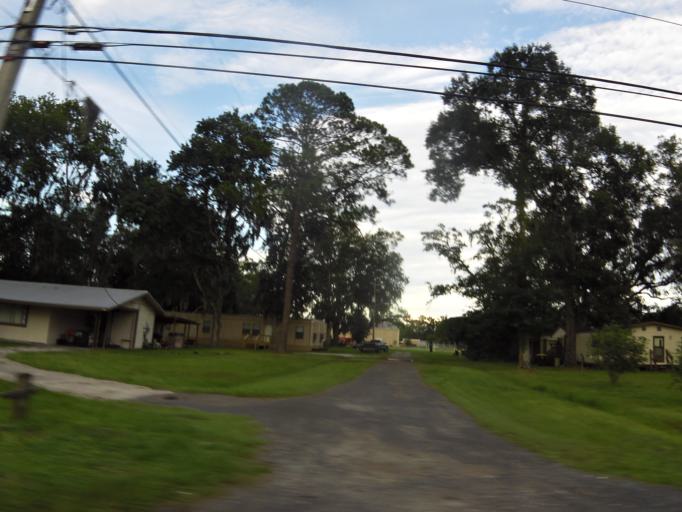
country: US
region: Florida
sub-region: Duval County
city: Jacksonville
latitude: 30.3296
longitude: -81.8066
